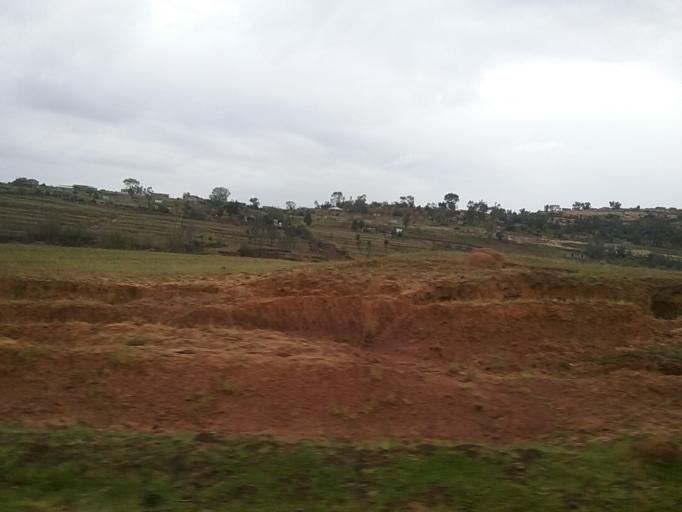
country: LS
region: Berea
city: Teyateyaneng
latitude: -29.1318
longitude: 27.7390
